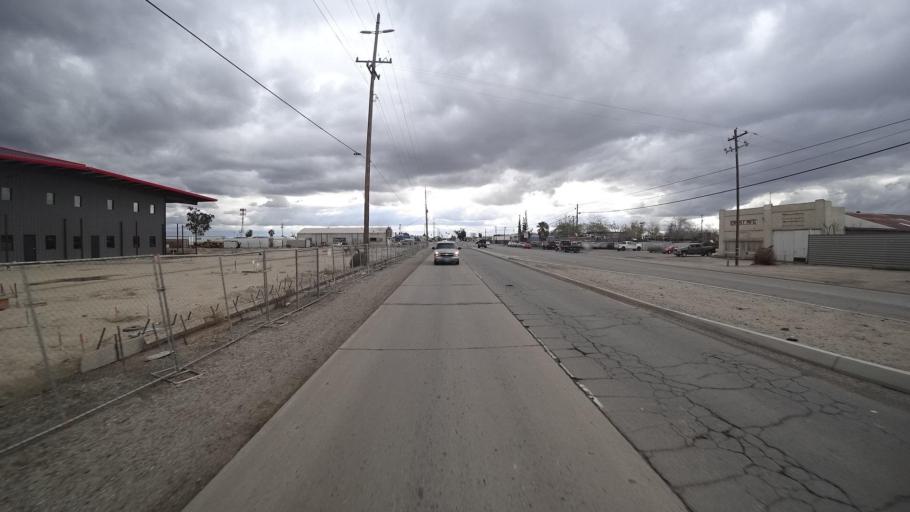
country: US
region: California
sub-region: Kern County
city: Bakersfield
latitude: 35.3275
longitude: -119.0030
